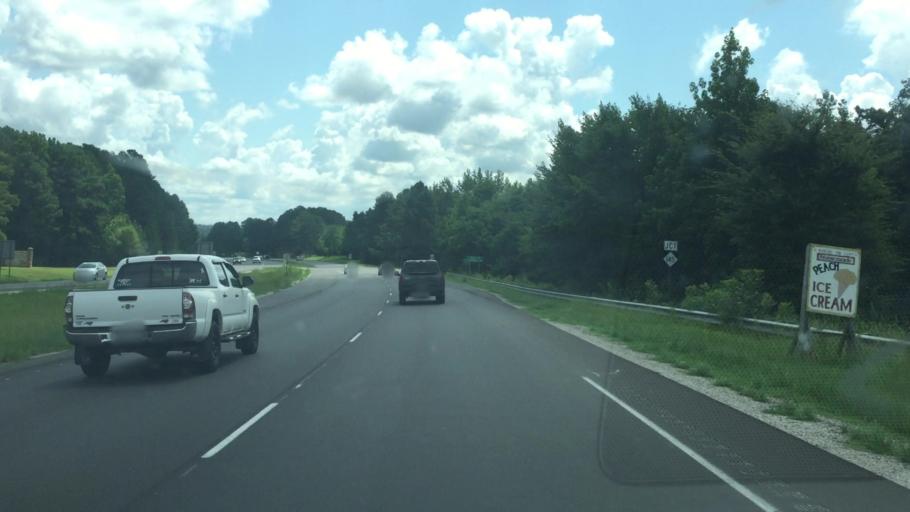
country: US
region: North Carolina
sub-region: Richmond County
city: Cordova
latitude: 34.9446
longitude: -79.8892
